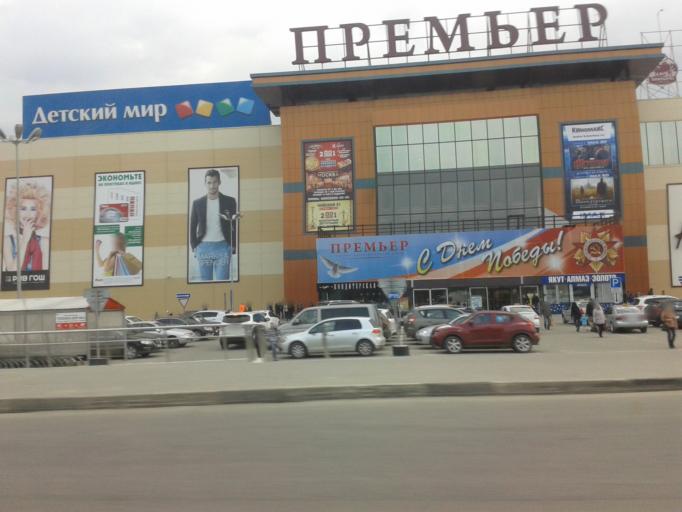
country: RU
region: Rjazan
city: Ryazan'
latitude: 54.6356
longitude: 39.6893
